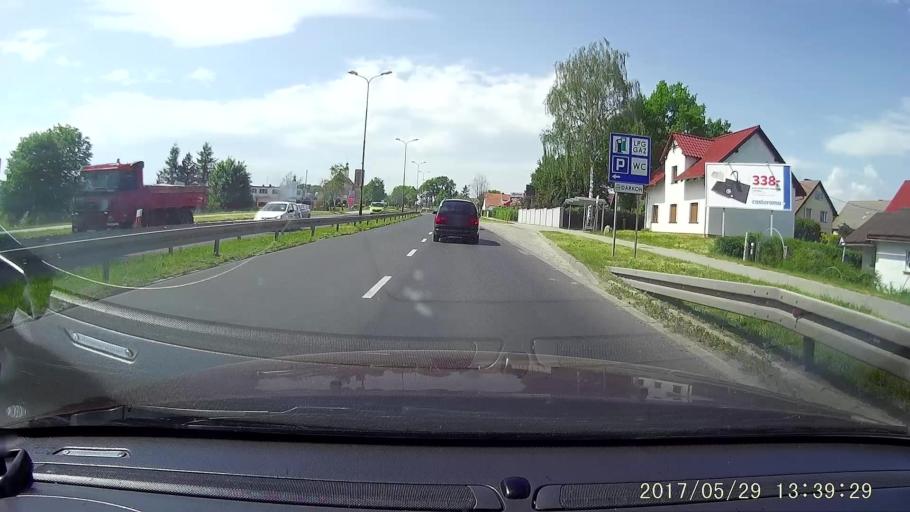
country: PL
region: Lower Silesian Voivodeship
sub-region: Powiat lubanski
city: Luban
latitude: 51.1276
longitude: 15.2863
